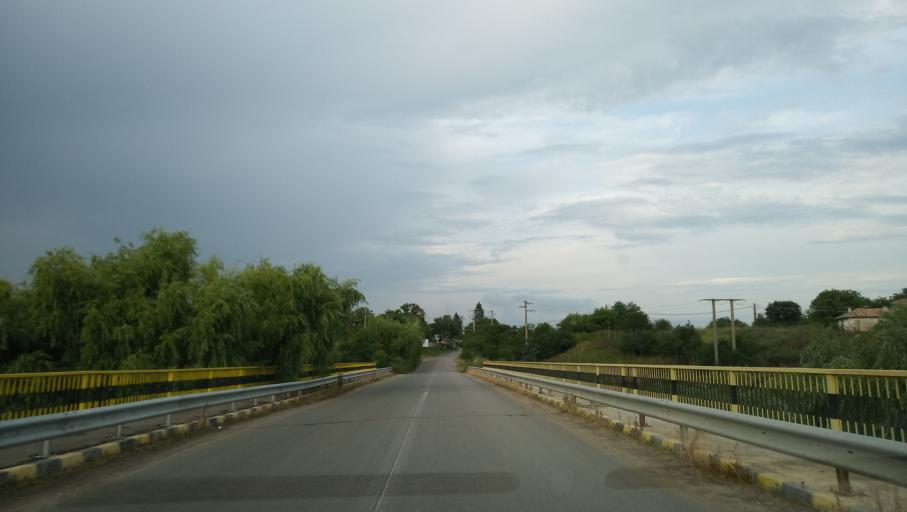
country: RO
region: Giurgiu
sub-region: Comuna Singureni
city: Singureni
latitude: 44.2316
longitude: 25.9388
